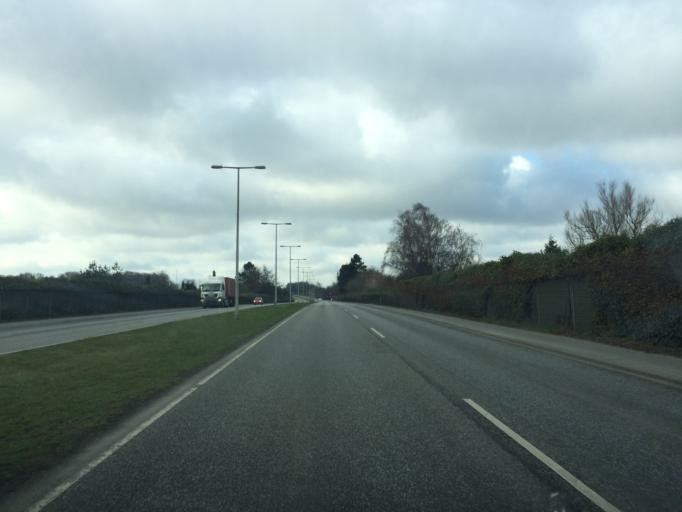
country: DK
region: South Denmark
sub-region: Fredericia Kommune
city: Snoghoj
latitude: 55.5468
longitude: 9.7223
